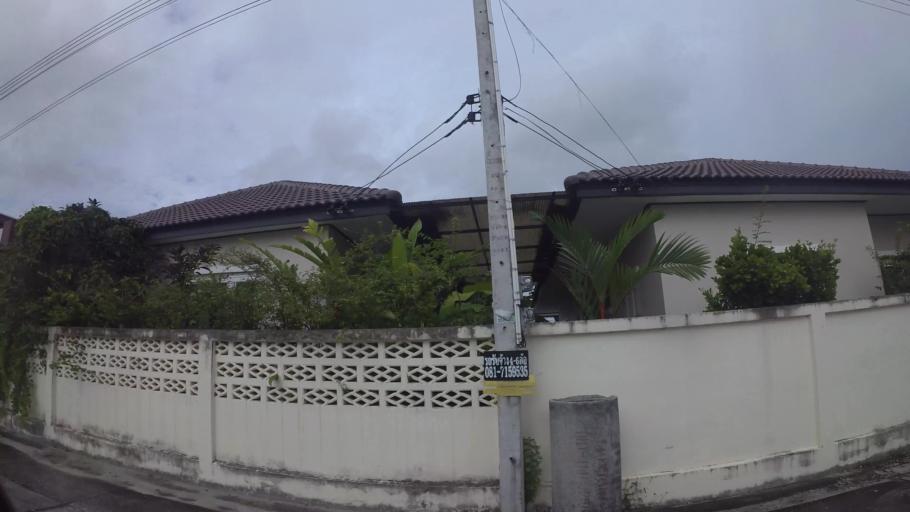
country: TH
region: Rayong
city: Rayong
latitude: 12.6683
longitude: 101.2814
